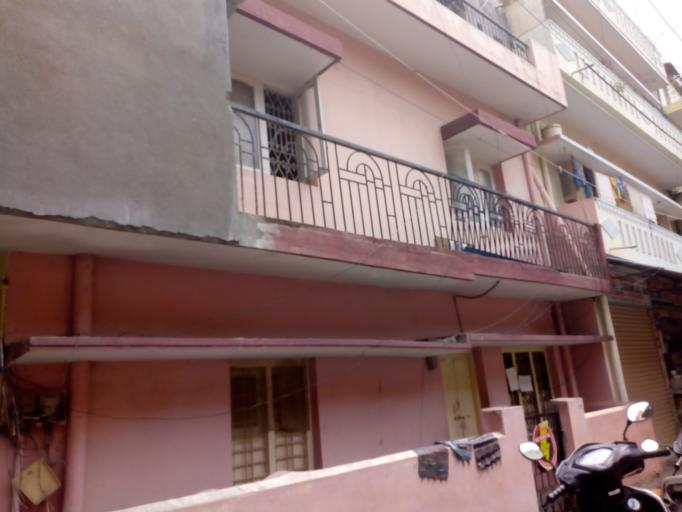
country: IN
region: Karnataka
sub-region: Bangalore Urban
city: Bangalore
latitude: 12.9727
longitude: 77.6494
